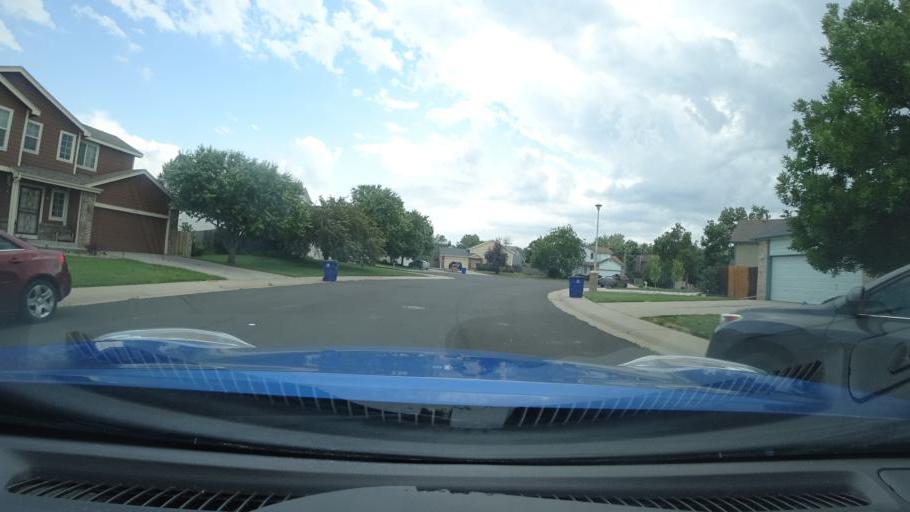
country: US
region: Colorado
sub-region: Adams County
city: Aurora
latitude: 39.6897
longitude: -104.7865
